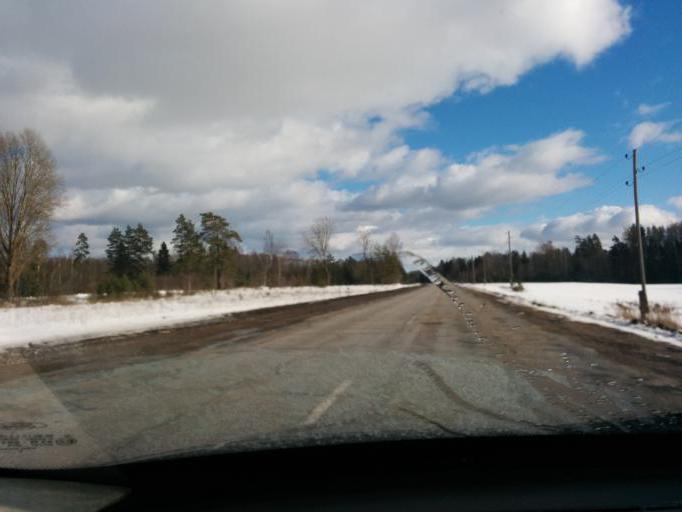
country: LV
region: Cesvaine
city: Cesvaine
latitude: 57.2373
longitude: 26.4208
